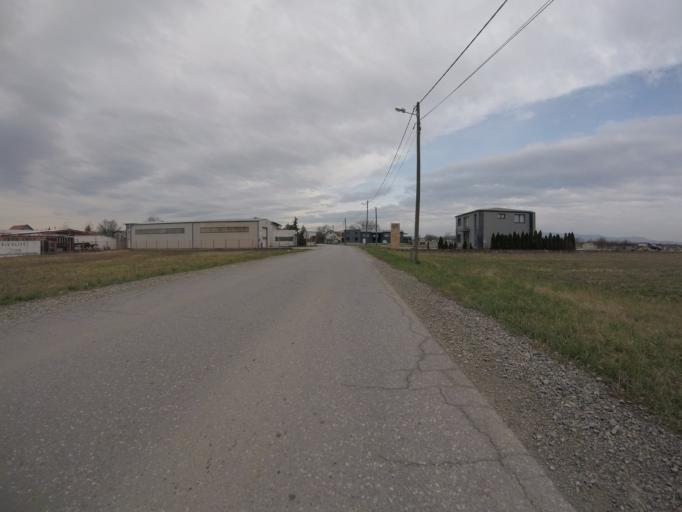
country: HR
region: Zagrebacka
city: Gradici
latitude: 45.7115
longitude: 16.0303
